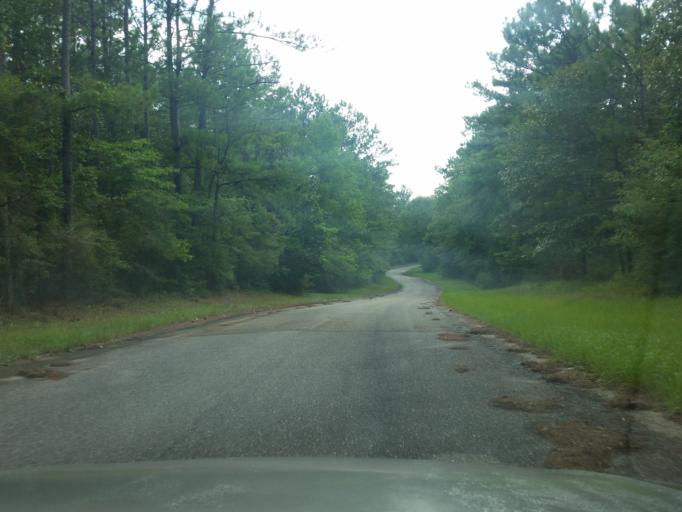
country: US
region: Alabama
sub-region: Baldwin County
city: Spanish Fort
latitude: 30.7316
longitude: -87.9089
